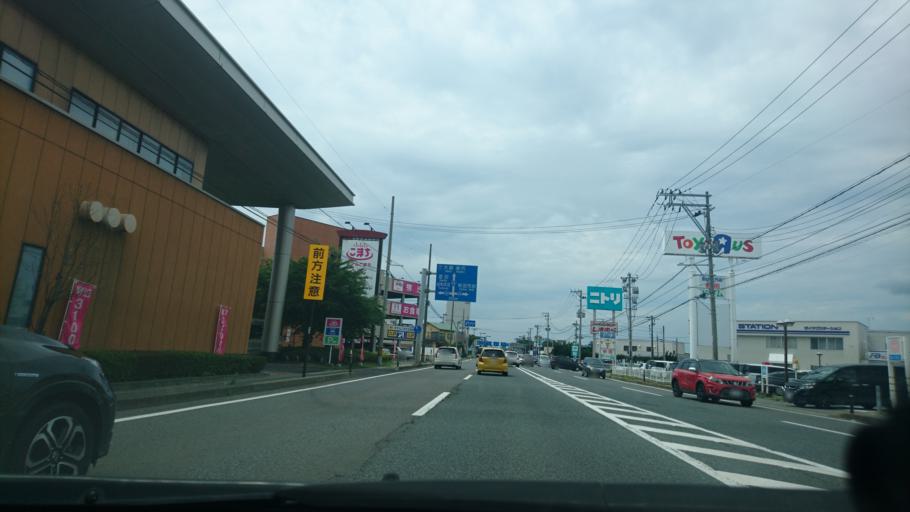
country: JP
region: Akita
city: Akita
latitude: 39.7017
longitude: 140.1085
